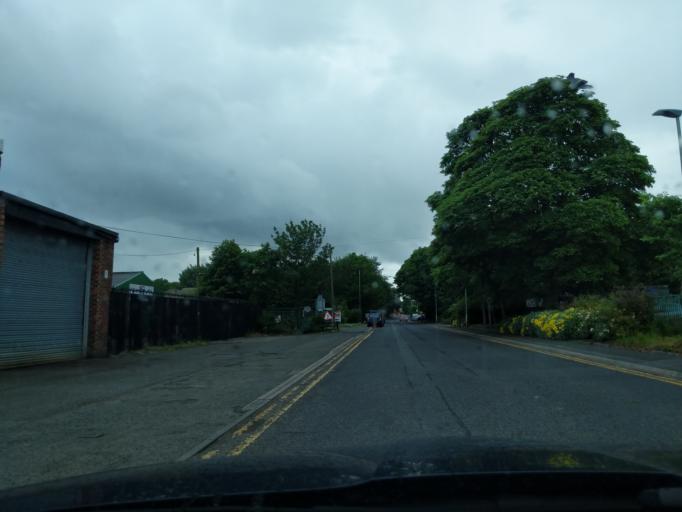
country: GB
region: England
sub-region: Northumberland
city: Seaton Delaval
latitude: 55.0778
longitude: -1.5349
